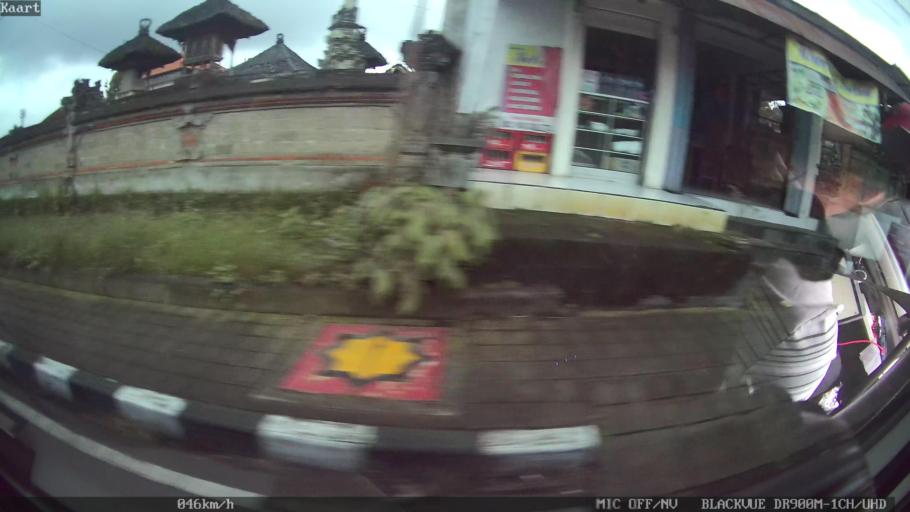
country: ID
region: Bali
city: Petang
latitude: -8.3939
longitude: 115.2187
